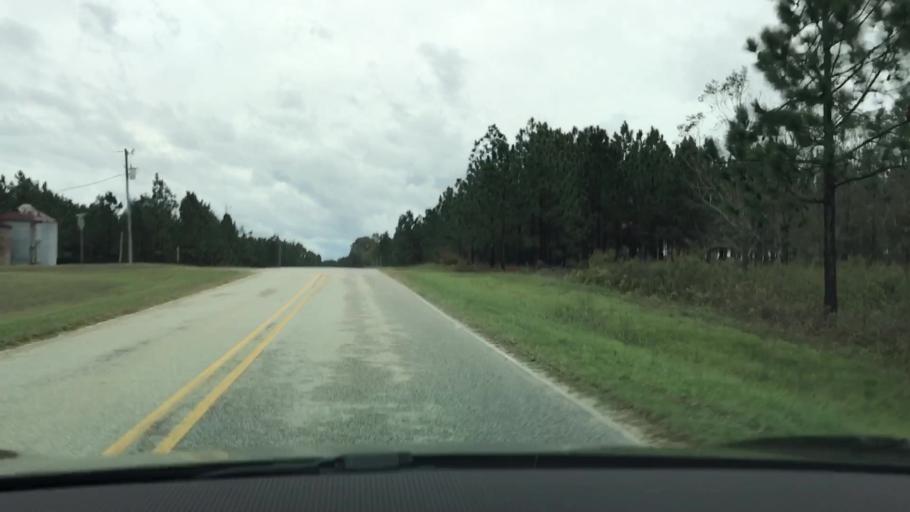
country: US
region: Georgia
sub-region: Jefferson County
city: Wadley
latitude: 32.8333
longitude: -82.3882
